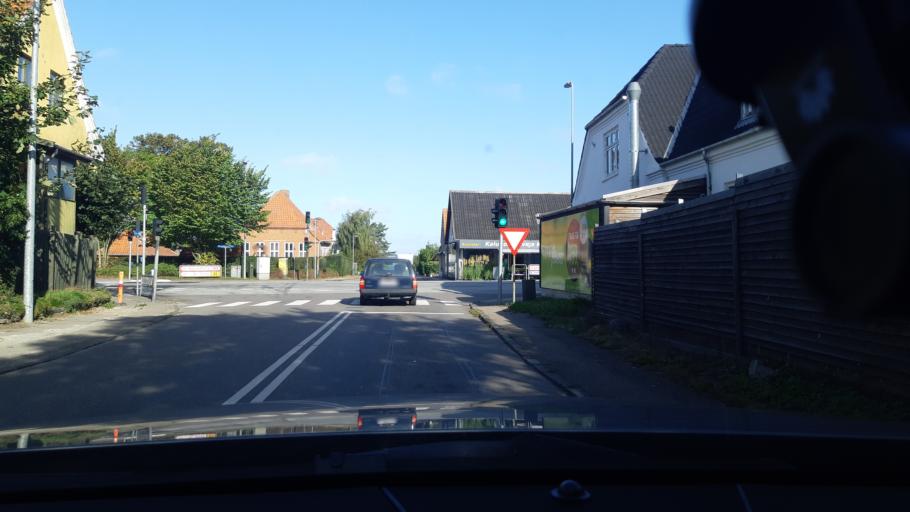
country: DK
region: Zealand
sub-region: Holbaek Kommune
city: Holbaek
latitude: 55.7158
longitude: 11.6880
